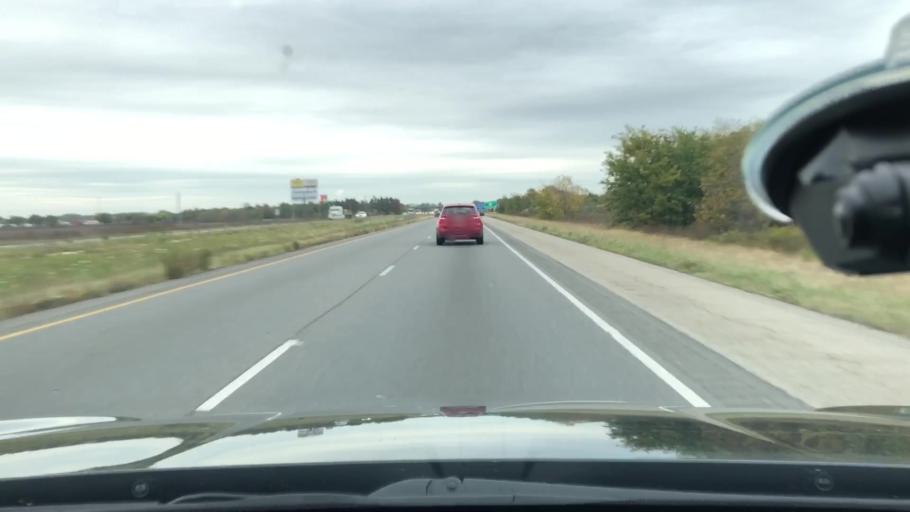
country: US
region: Arkansas
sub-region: Miller County
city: Texarkana
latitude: 33.5052
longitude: -93.9521
